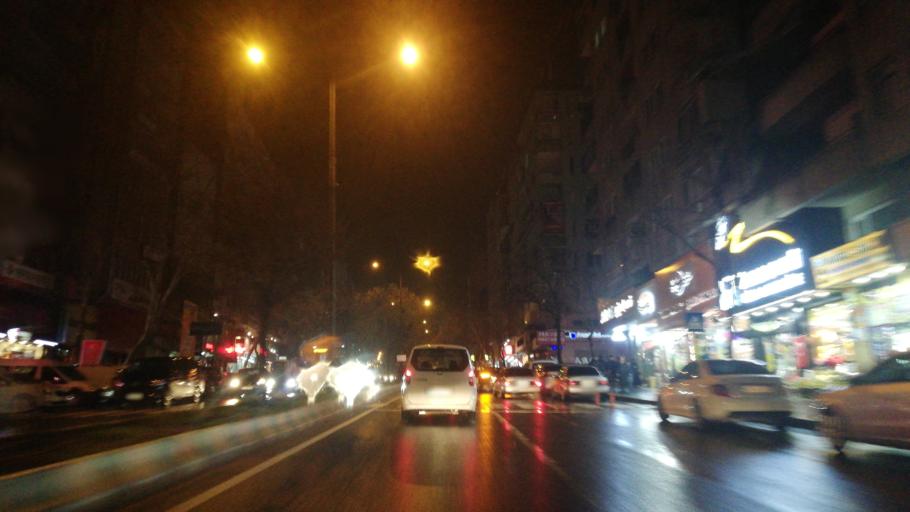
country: TR
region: Kahramanmaras
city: Kahramanmaras
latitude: 37.5779
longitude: 36.9281
